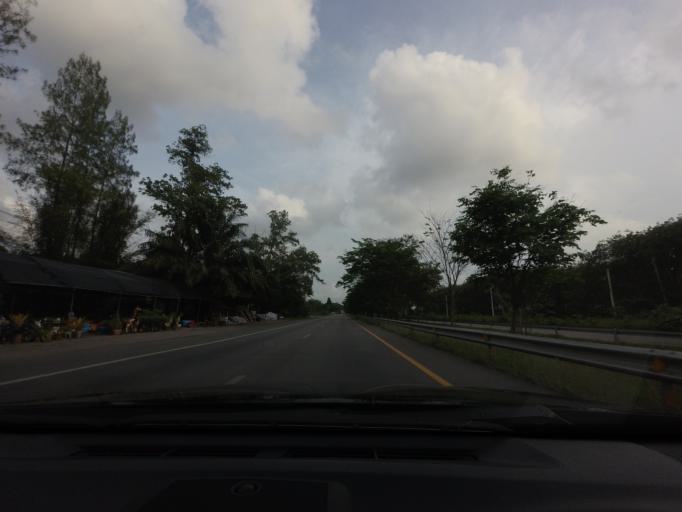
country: TH
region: Chumphon
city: Lamae
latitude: 9.8054
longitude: 99.0688
